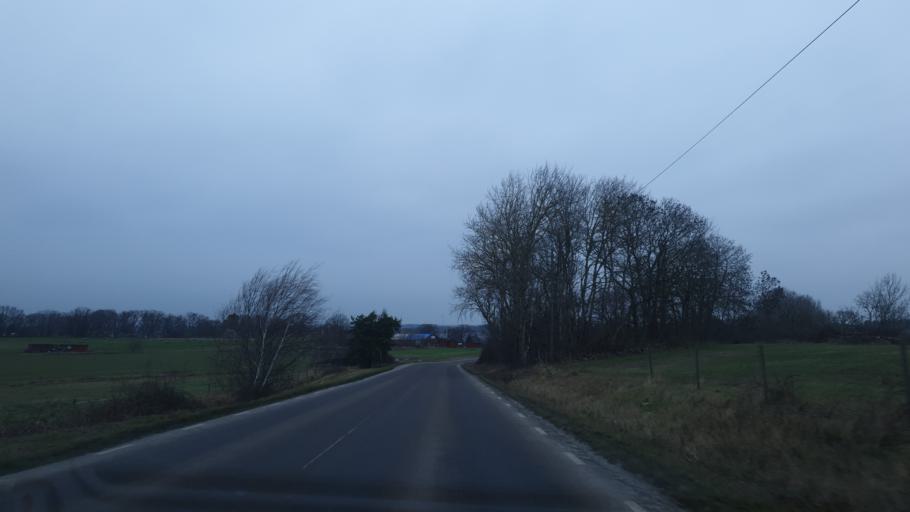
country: SE
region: Blekinge
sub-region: Karlskrona Kommun
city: Sturko
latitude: 56.1343
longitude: 15.7404
